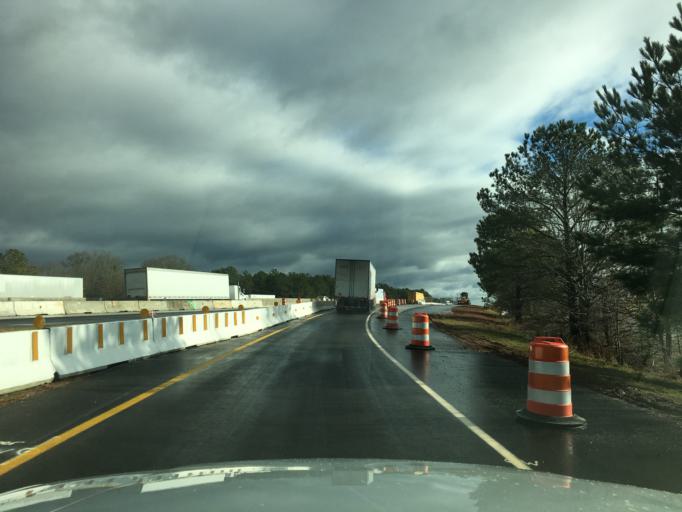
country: US
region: South Carolina
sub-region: Spartanburg County
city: Mayo
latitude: 35.0268
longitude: -81.8735
